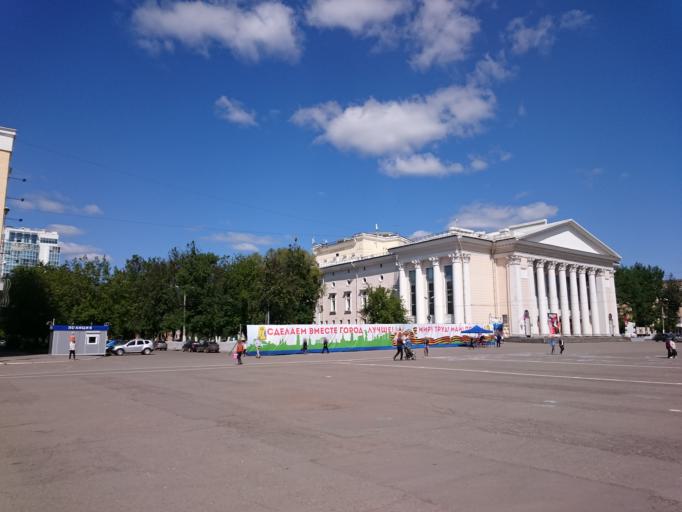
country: RU
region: Kirov
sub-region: Kirovo-Chepetskiy Rayon
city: Kirov
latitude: 58.6038
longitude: 49.6665
